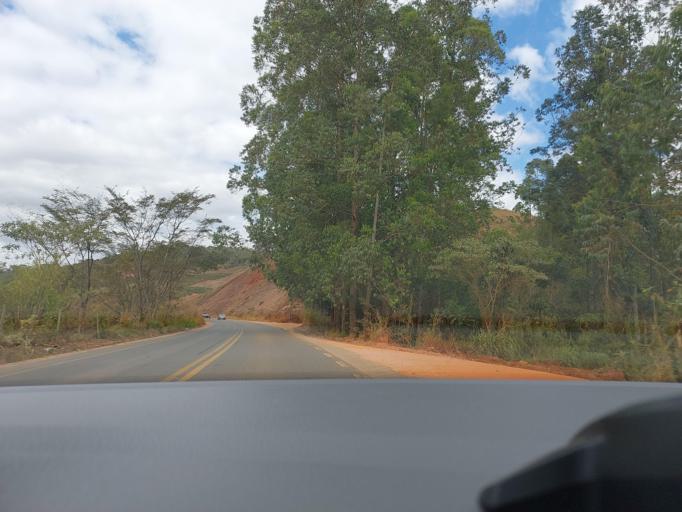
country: BR
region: Minas Gerais
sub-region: Vicosa
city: Vicosa
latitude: -20.8426
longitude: -42.6870
